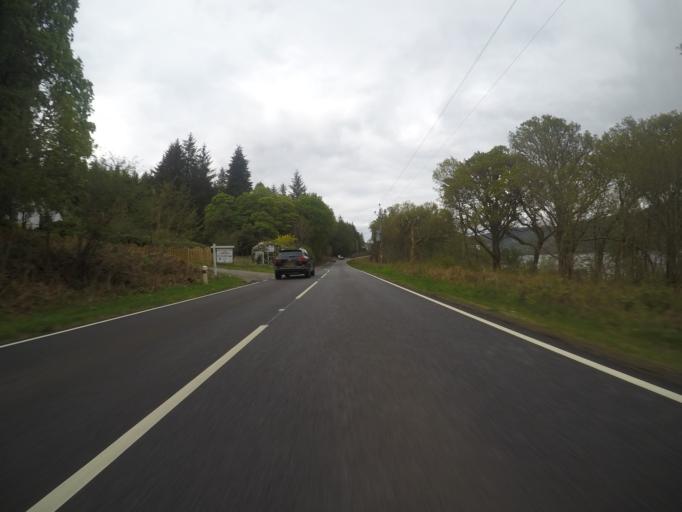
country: GB
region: Scotland
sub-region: Highland
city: Beauly
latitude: 57.1853
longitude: -4.6230
